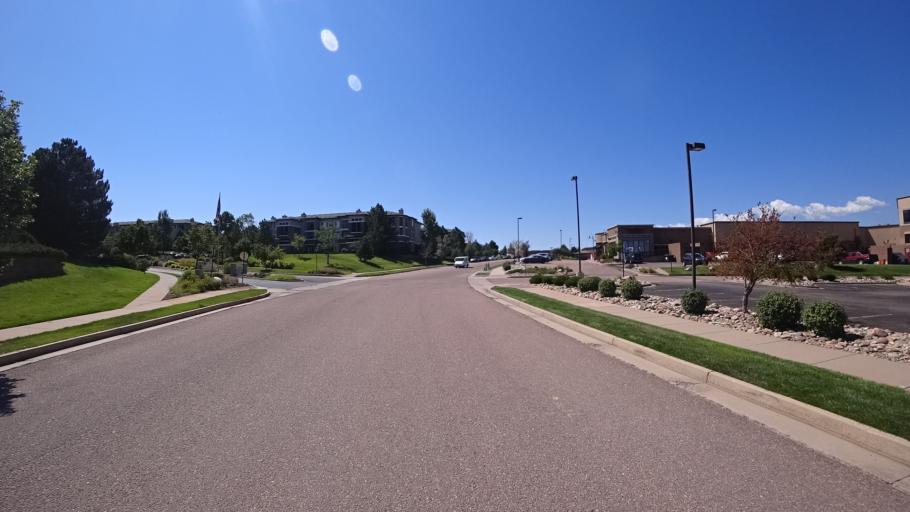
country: US
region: Colorado
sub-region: El Paso County
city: Air Force Academy
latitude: 38.9685
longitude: -104.7819
